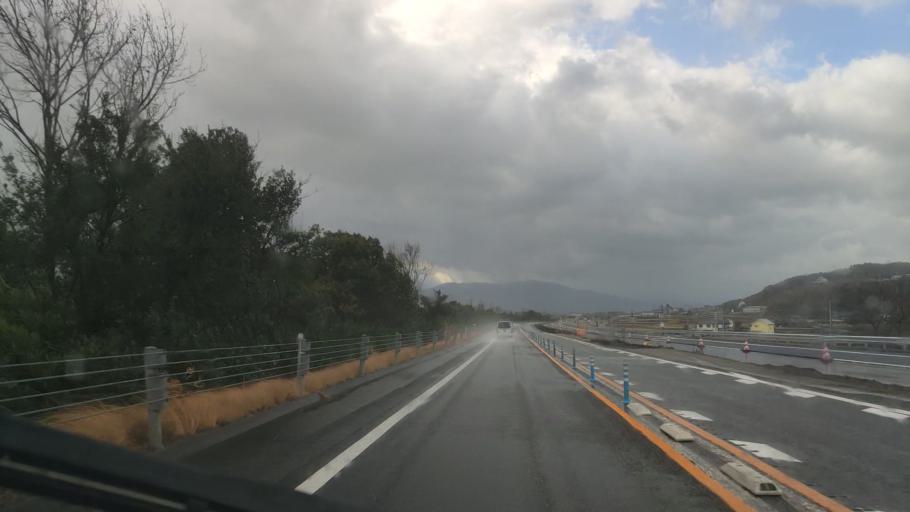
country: JP
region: Tokushima
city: Wakimachi
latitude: 34.0965
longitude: 134.2225
